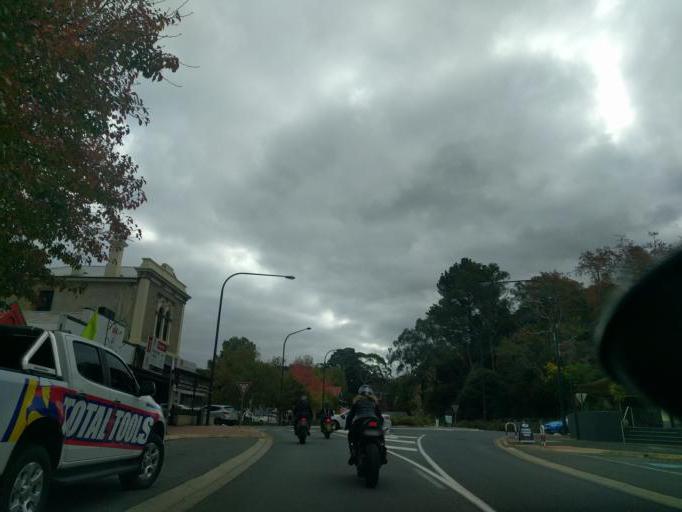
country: AU
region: South Australia
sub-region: Adelaide Hills
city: Stirling
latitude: -35.0155
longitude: 138.7369
